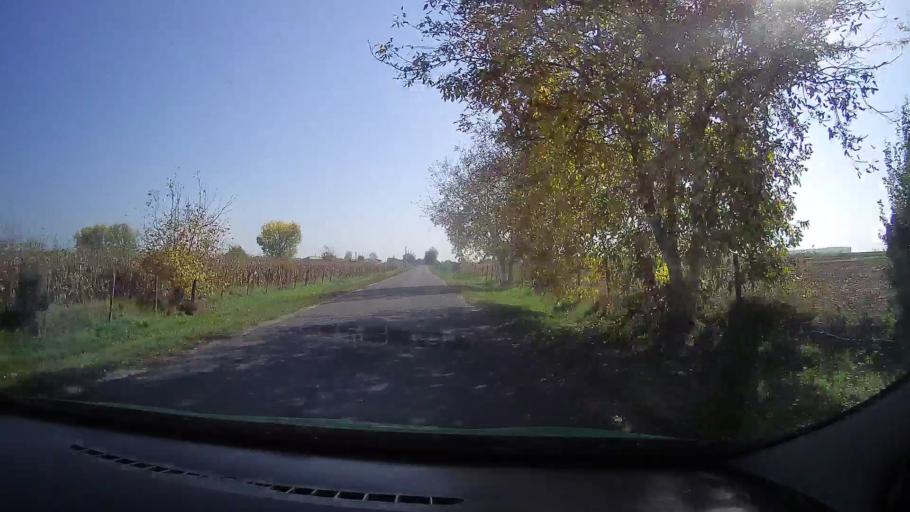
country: RO
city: Foieni
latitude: 47.6964
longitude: 22.3637
